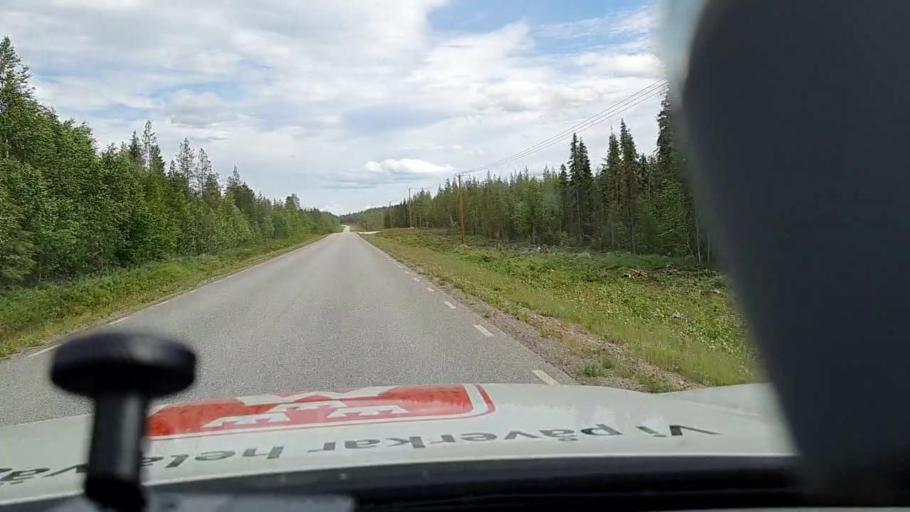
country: SE
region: Norrbotten
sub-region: Jokkmokks Kommun
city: Jokkmokk
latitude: 66.6567
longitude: 19.9734
